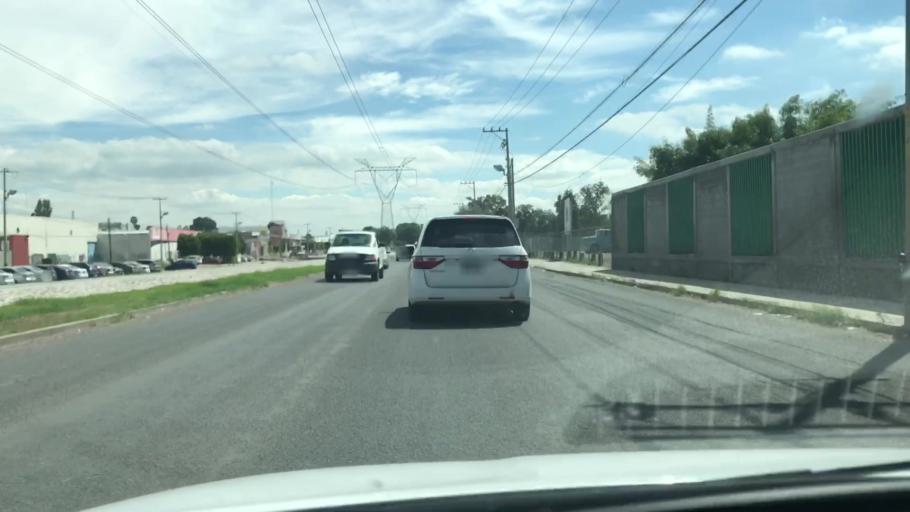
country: MX
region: Guanajuato
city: Celaya
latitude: 20.5520
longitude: -100.8182
